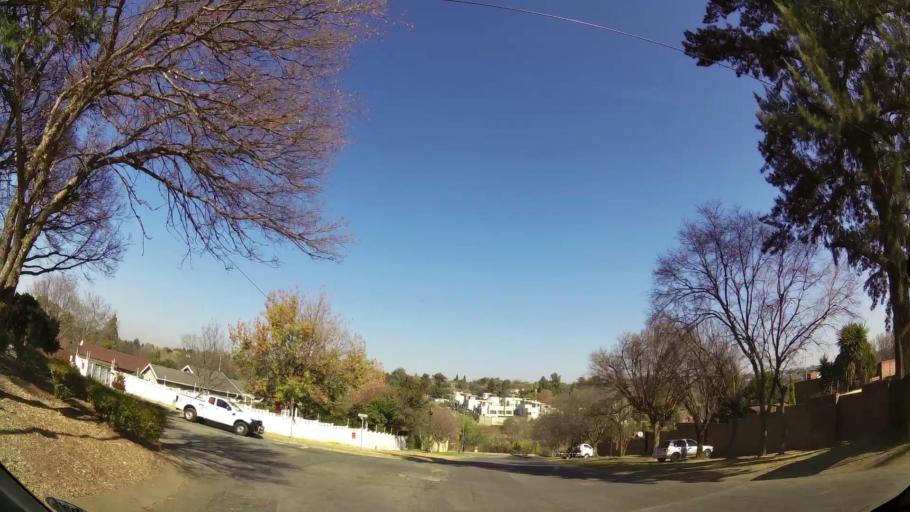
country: ZA
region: Gauteng
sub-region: City of Johannesburg Metropolitan Municipality
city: Midrand
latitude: -26.0487
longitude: 28.0521
